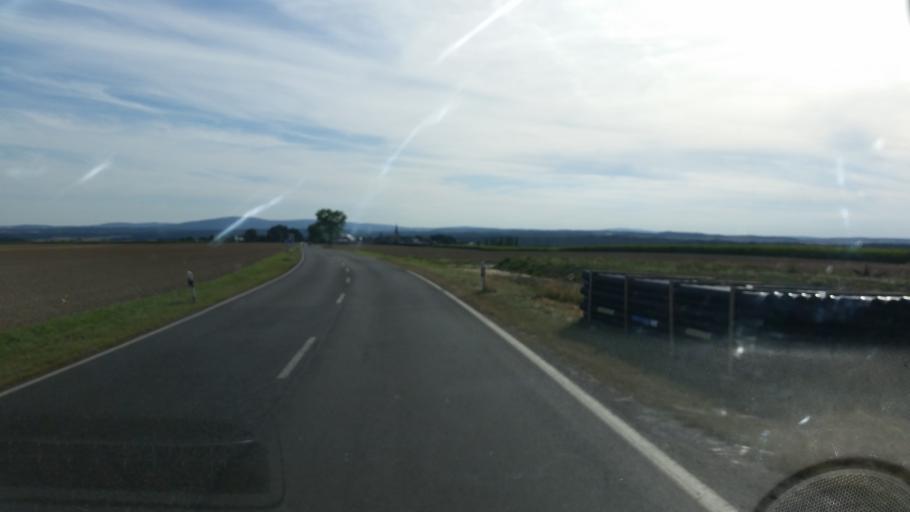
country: DE
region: Rheinland-Pfalz
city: Kappel
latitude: 50.0094
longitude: 7.3690
